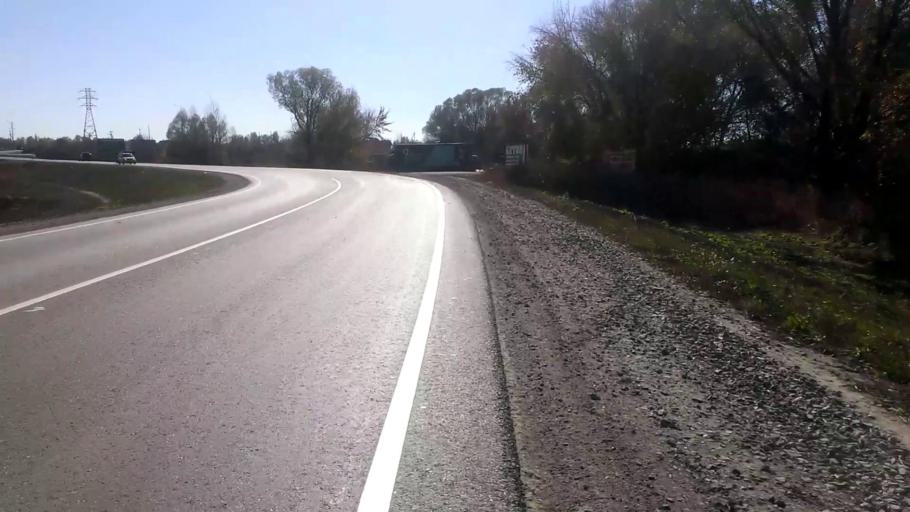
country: RU
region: Altai Krai
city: Sannikovo
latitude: 53.3223
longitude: 83.9427
